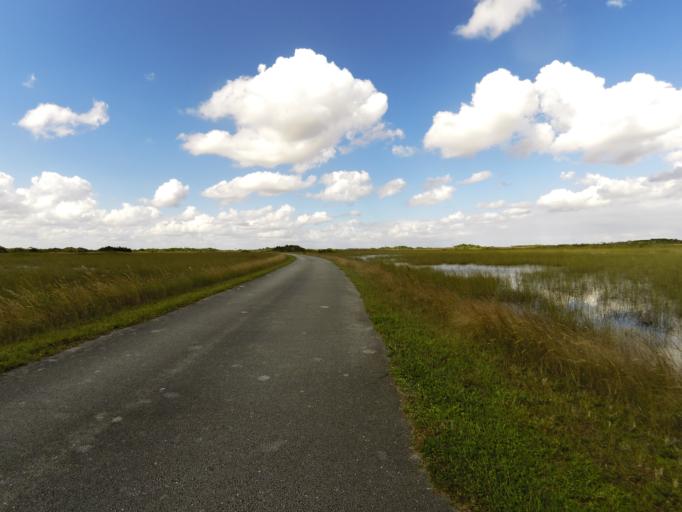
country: US
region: Florida
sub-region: Miami-Dade County
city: The Hammocks
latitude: 25.7041
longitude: -80.7607
